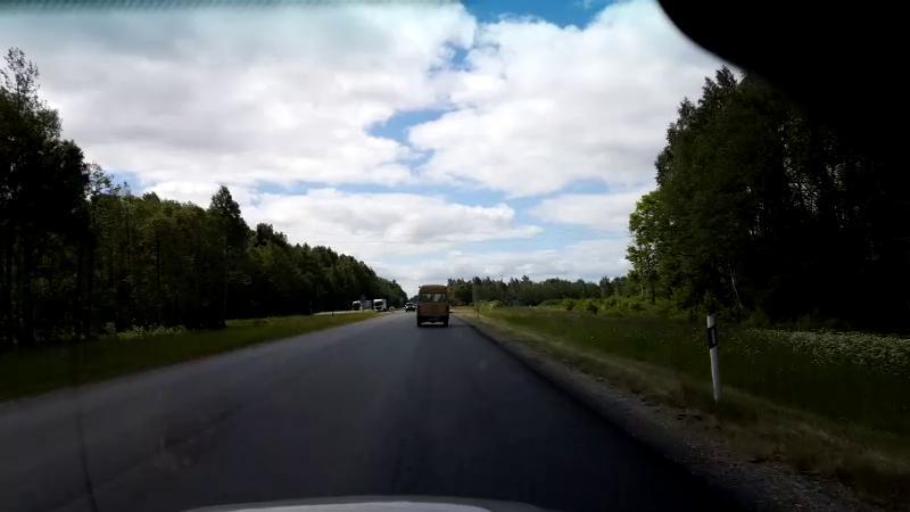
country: LV
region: Salacgrivas
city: Ainazi
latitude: 57.9674
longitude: 24.4483
